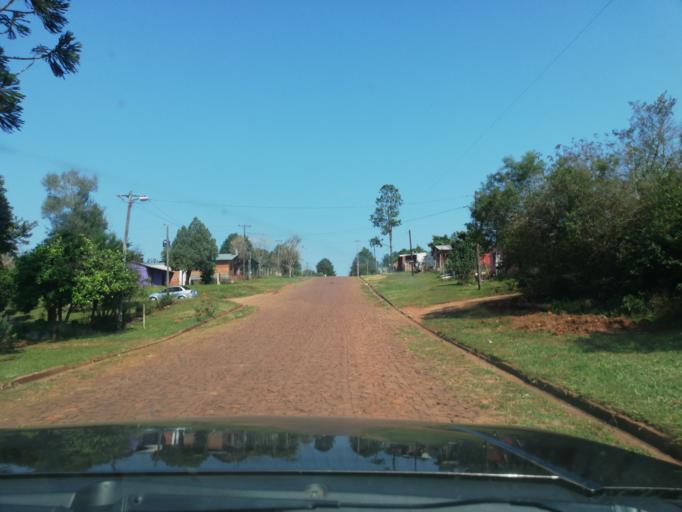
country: AR
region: Misiones
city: Bonpland
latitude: -27.4777
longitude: -55.4773
